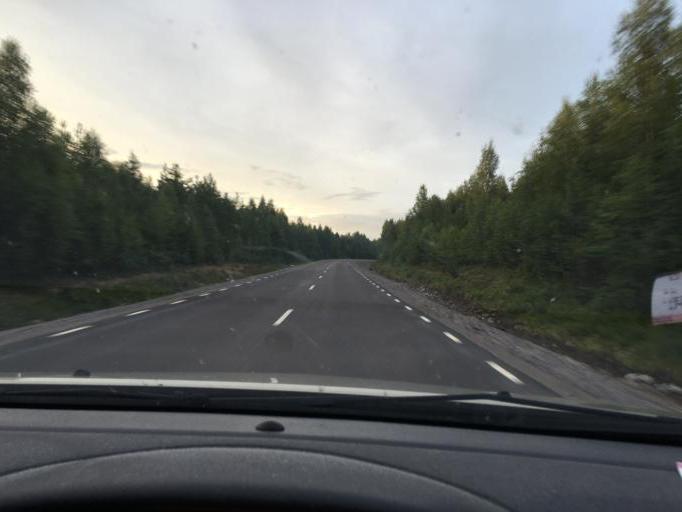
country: SE
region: Norrbotten
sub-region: Lulea Kommun
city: Ranea
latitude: 66.0479
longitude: 22.2052
